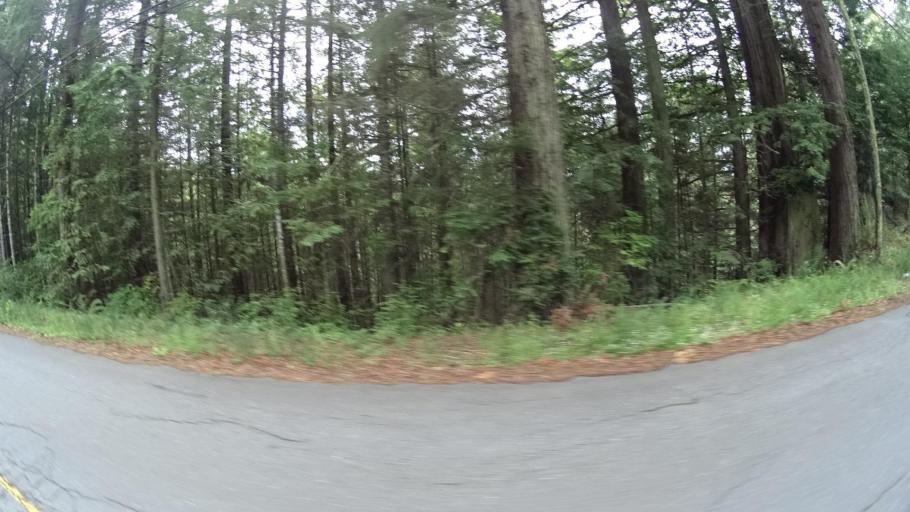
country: US
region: California
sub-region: Humboldt County
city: Bayside
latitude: 40.7868
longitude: -124.0600
